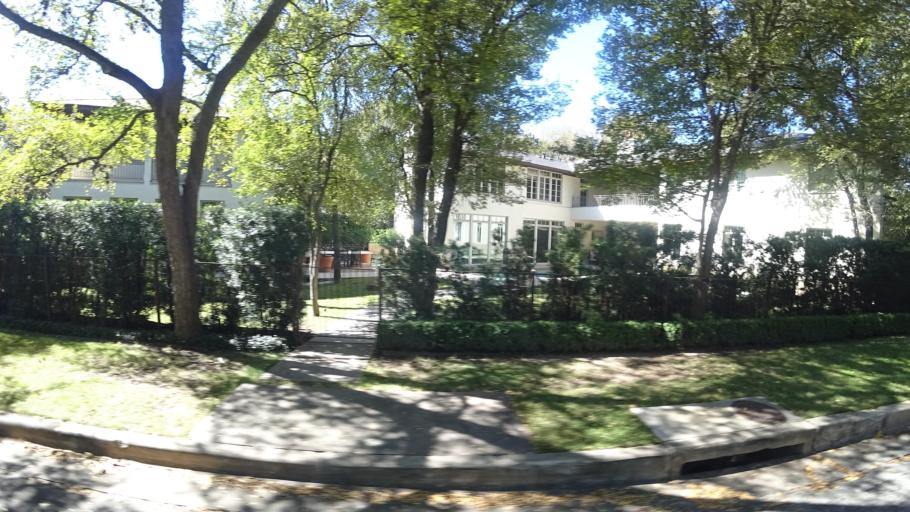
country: US
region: Texas
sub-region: Travis County
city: Rollingwood
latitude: 30.2916
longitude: -97.7676
